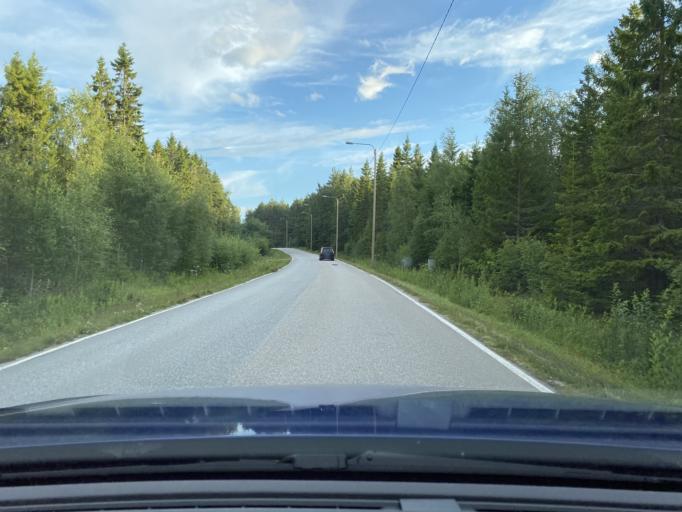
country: FI
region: Ostrobothnia
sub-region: Vaasa
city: Korsnaes
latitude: 62.9542
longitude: 21.1777
